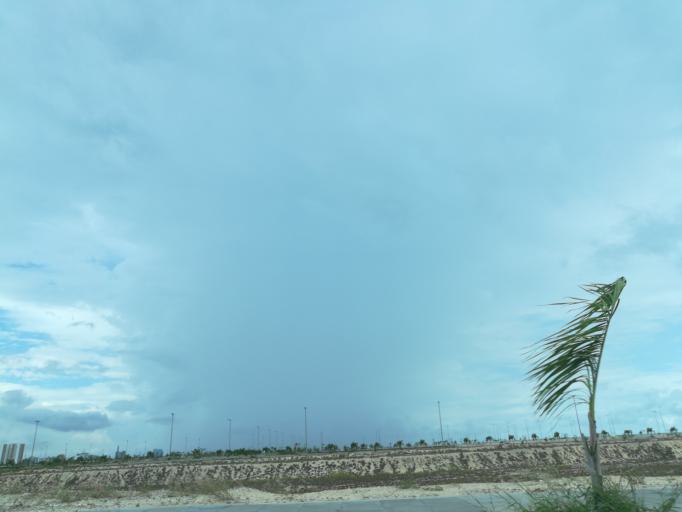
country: NG
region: Lagos
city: Ikoyi
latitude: 6.4059
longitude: 3.4154
